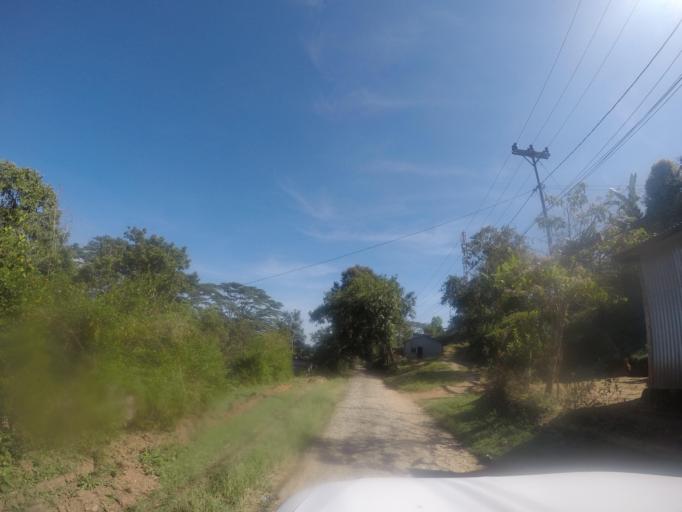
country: TL
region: Ermera
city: Gleno
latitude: -8.7304
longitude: 125.4375
